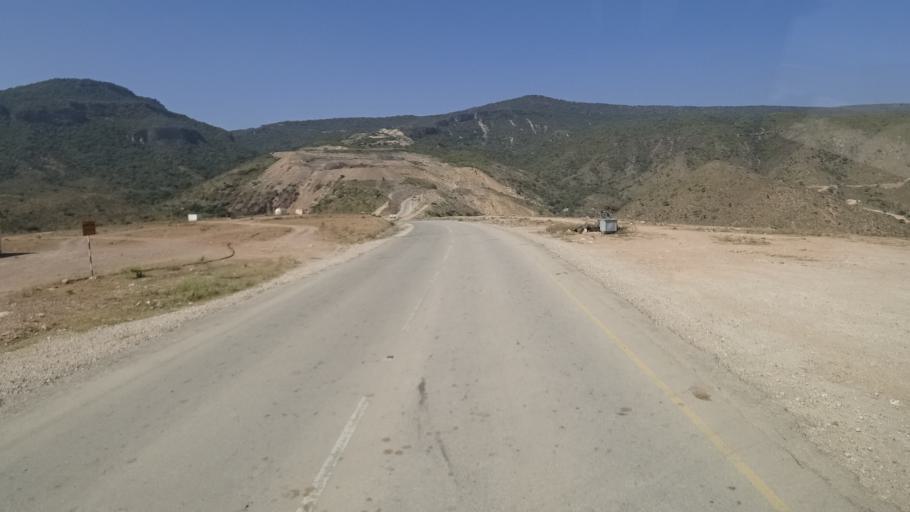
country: OM
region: Zufar
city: Salalah
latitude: 17.0391
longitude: 54.6130
